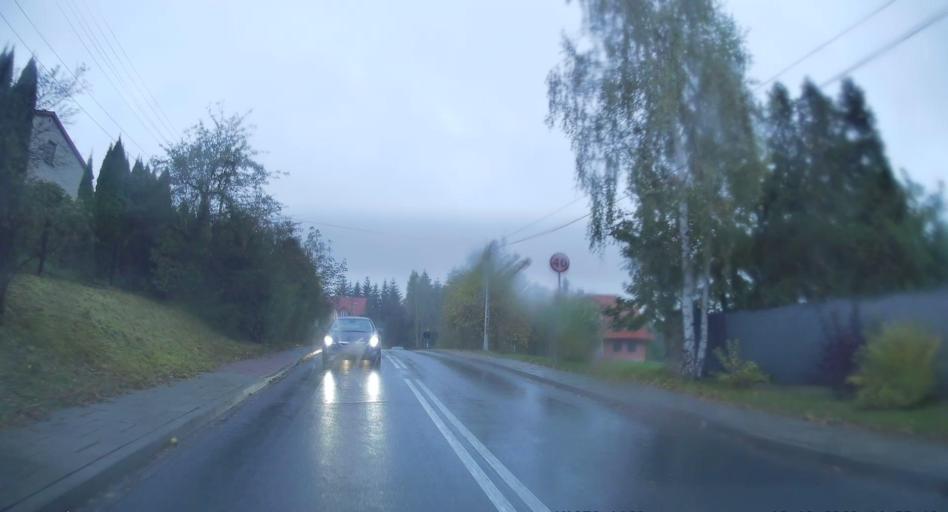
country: PL
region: Lesser Poland Voivodeship
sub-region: Powiat krakowski
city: Ochojno
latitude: 49.9734
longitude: 19.9871
